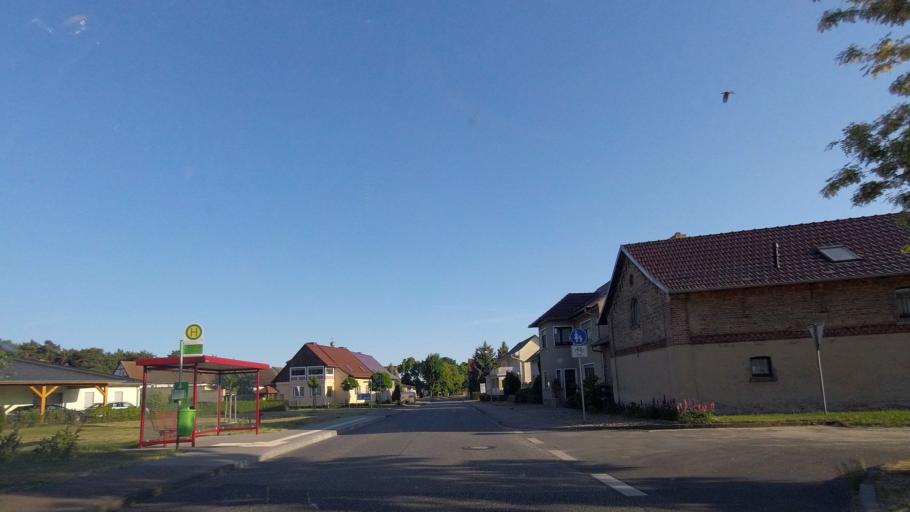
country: DE
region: Brandenburg
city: Golzow
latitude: 52.2911
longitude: 12.6014
